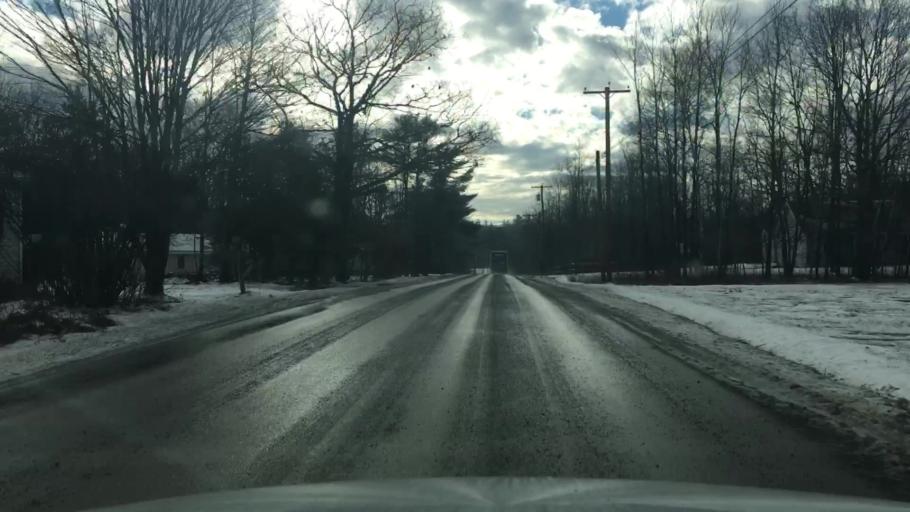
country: US
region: Maine
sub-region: Penobscot County
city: Orrington
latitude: 44.7253
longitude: -68.7558
